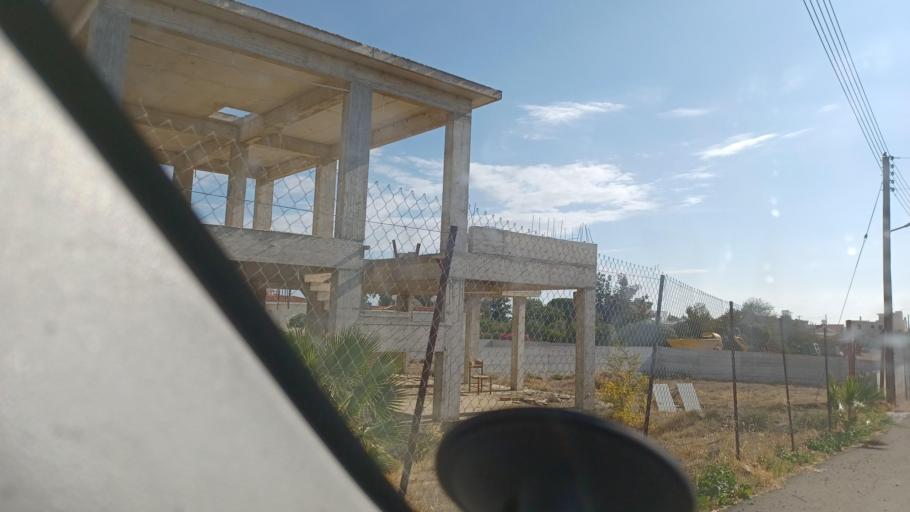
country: CY
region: Pafos
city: Mesogi
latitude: 34.7433
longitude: 32.5341
